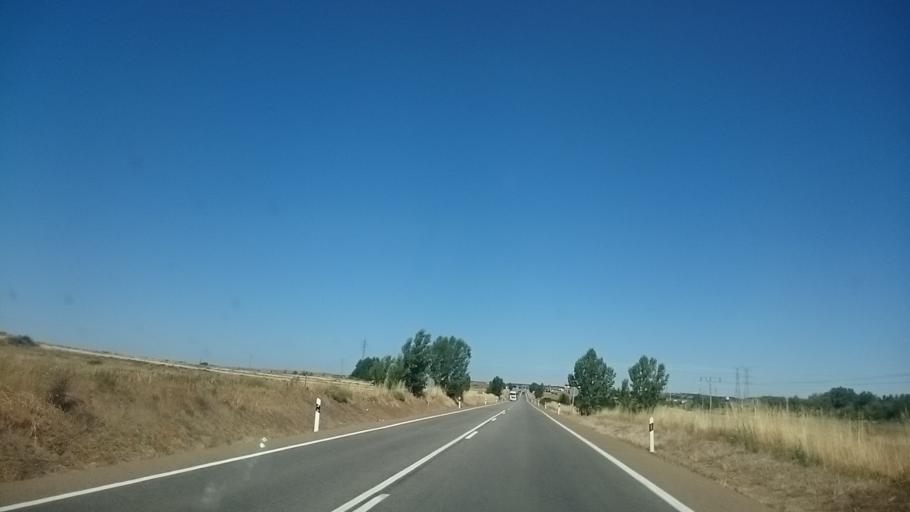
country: ES
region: Castille and Leon
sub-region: Provincia de Leon
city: Villaturiel
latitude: 42.5555
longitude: -5.4732
